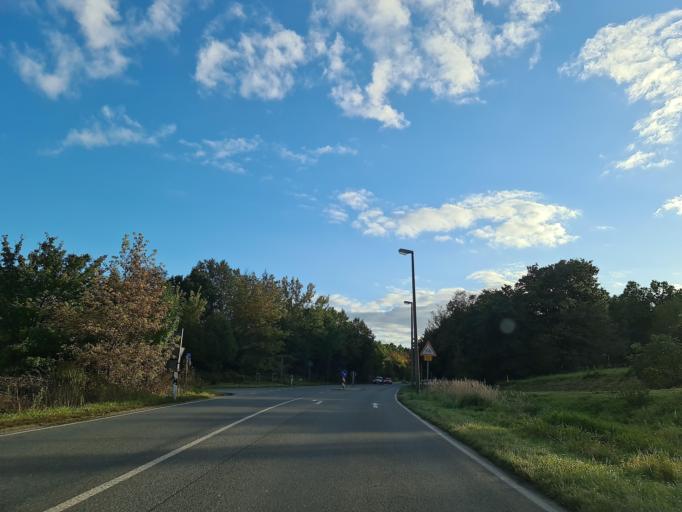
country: DE
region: Thuringia
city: Gera
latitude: 50.8446
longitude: 12.0779
